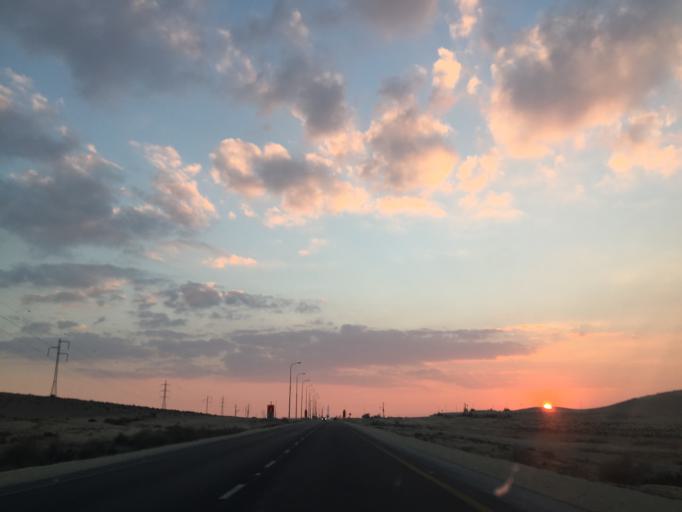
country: IL
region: Southern District
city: Yeroham
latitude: 31.0274
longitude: 34.7977
